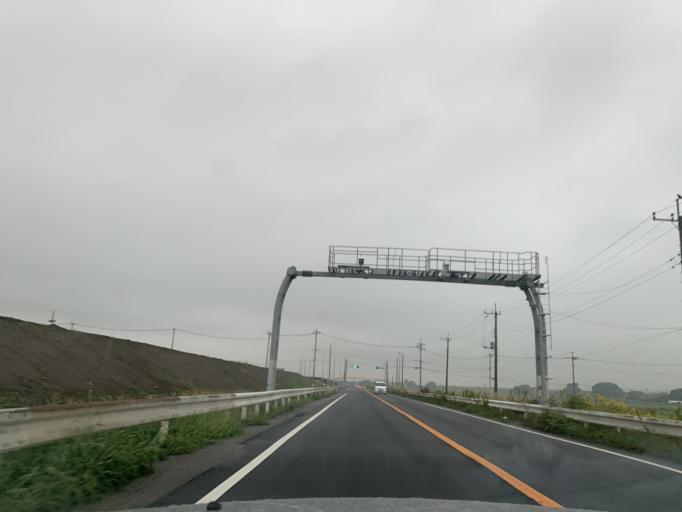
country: JP
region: Chiba
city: Nagareyama
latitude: 35.8986
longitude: 139.8921
